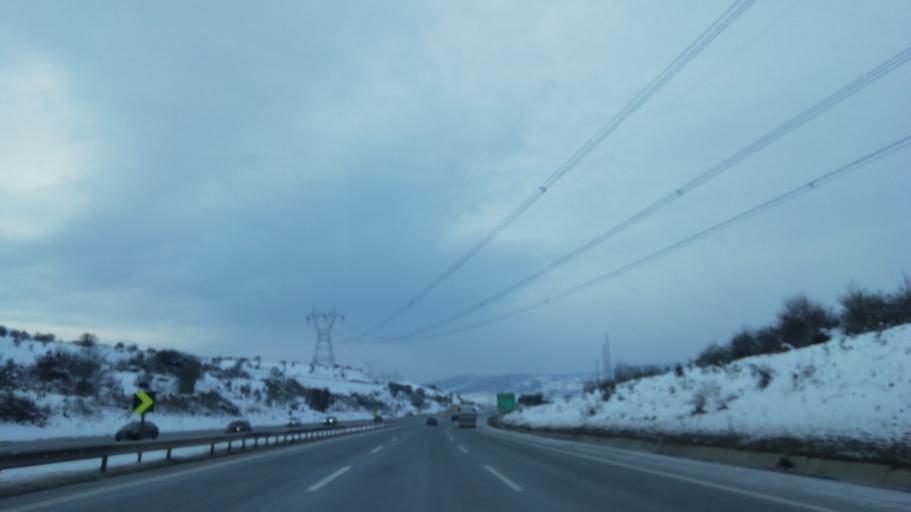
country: TR
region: Bolu
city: Yenicaga
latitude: 40.7648
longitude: 32.0416
